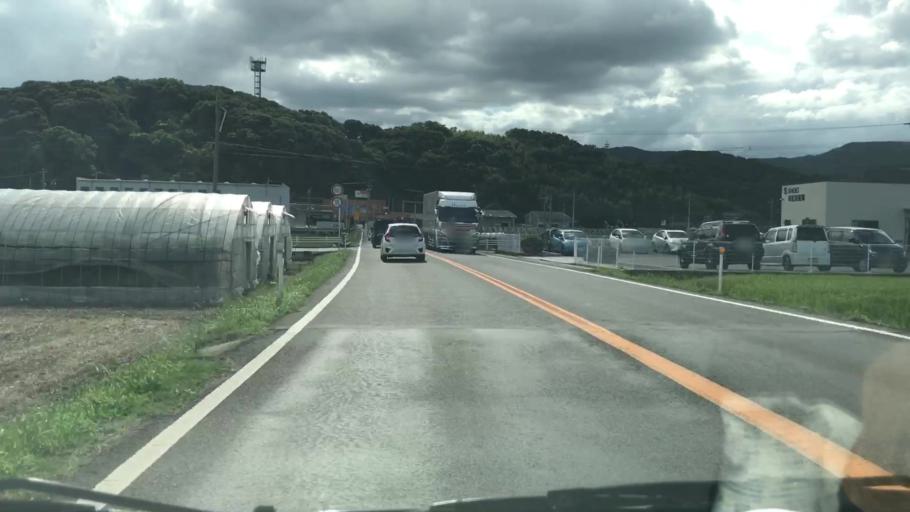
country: JP
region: Saga Prefecture
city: Kashima
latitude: 33.1391
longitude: 130.1250
